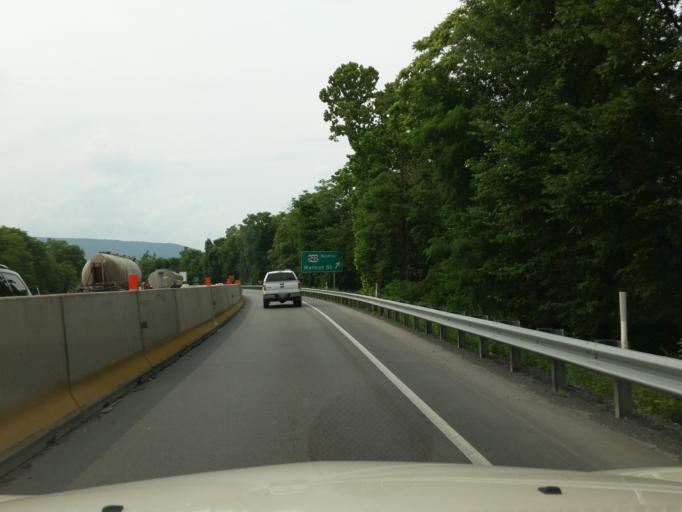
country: US
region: Pennsylvania
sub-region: Mifflin County
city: Lewistown
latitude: 40.6029
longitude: -77.5623
